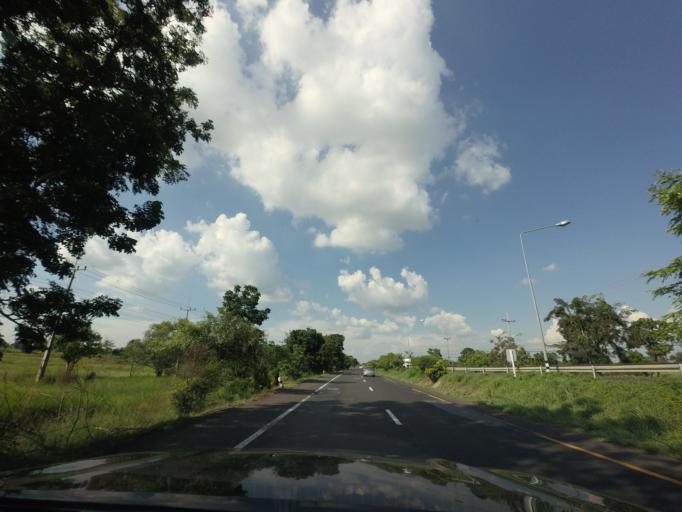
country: TH
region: Nakhon Ratchasima
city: Bua Lai
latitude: 15.6844
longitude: 102.5779
